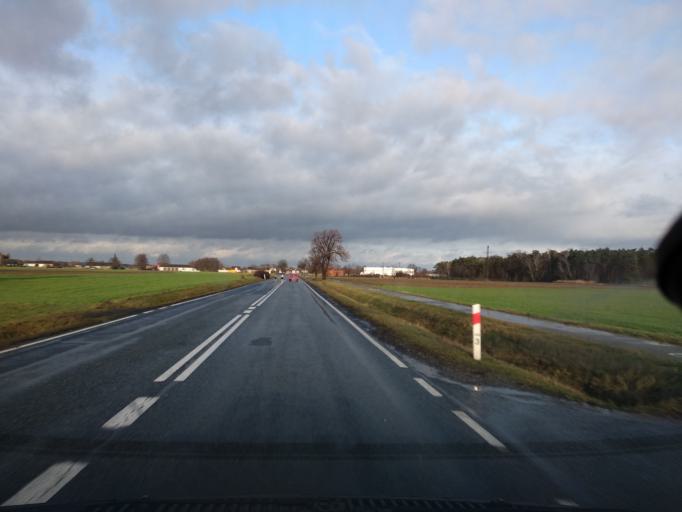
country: PL
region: Greater Poland Voivodeship
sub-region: Powiat koninski
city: Rychwal
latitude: 52.0888
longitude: 18.1640
